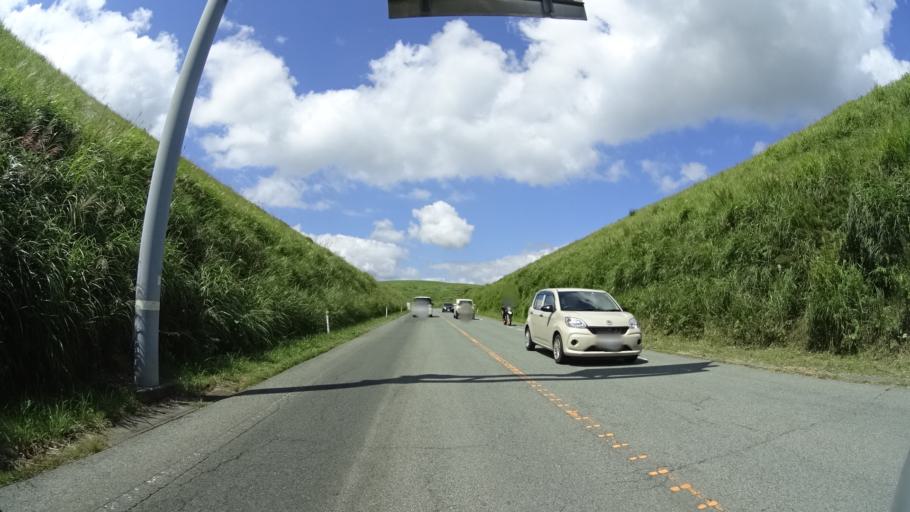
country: JP
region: Kumamoto
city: Aso
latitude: 33.0019
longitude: 131.1389
